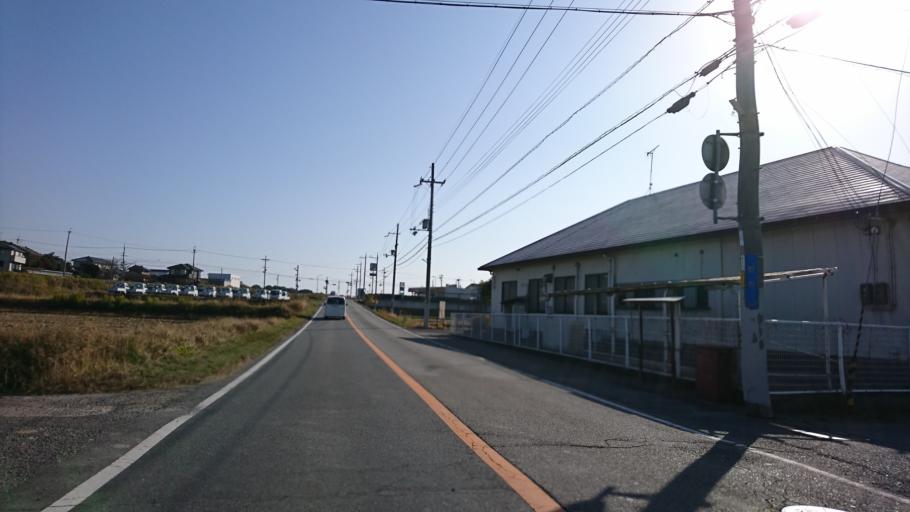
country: JP
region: Hyogo
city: Miki
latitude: 34.7610
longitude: 134.9399
